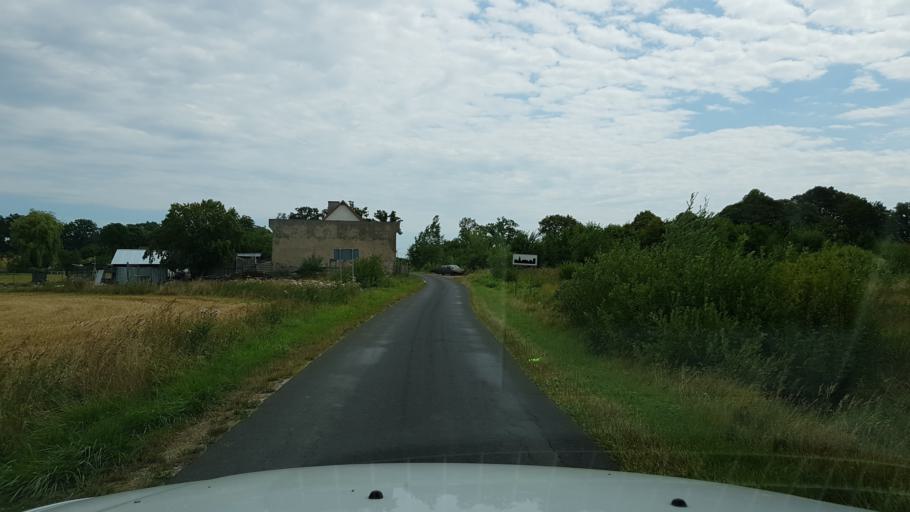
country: PL
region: West Pomeranian Voivodeship
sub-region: Powiat koszalinski
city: Mielno
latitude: 54.1714
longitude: 16.0482
